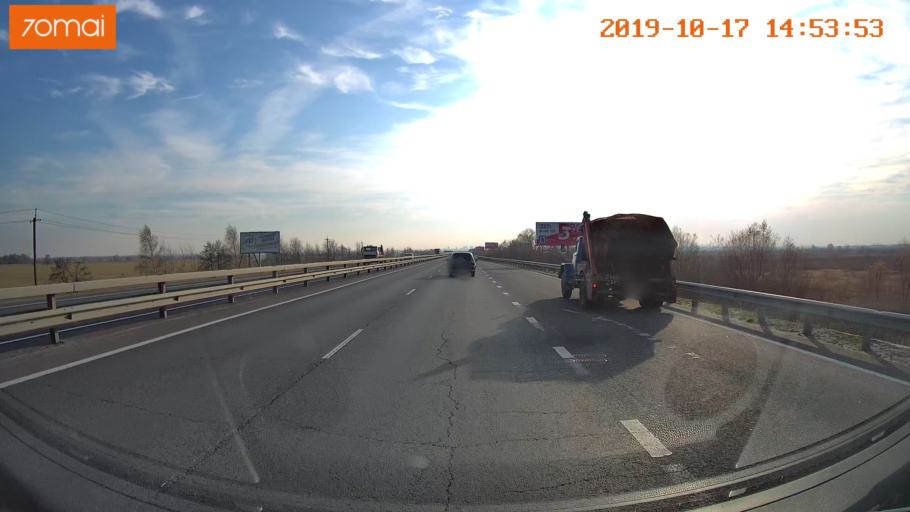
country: RU
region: Rjazan
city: Polyany
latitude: 54.6885
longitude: 39.8358
